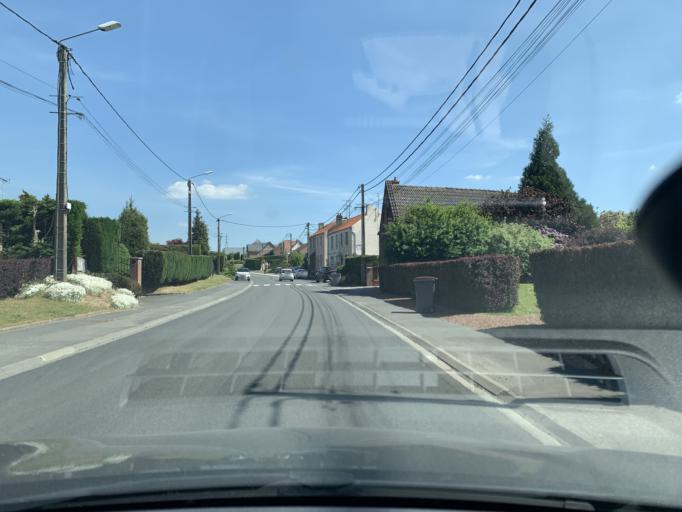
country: FR
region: Nord-Pas-de-Calais
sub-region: Departement du Nord
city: Fontaine-au-Pire
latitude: 50.1298
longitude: 3.3864
